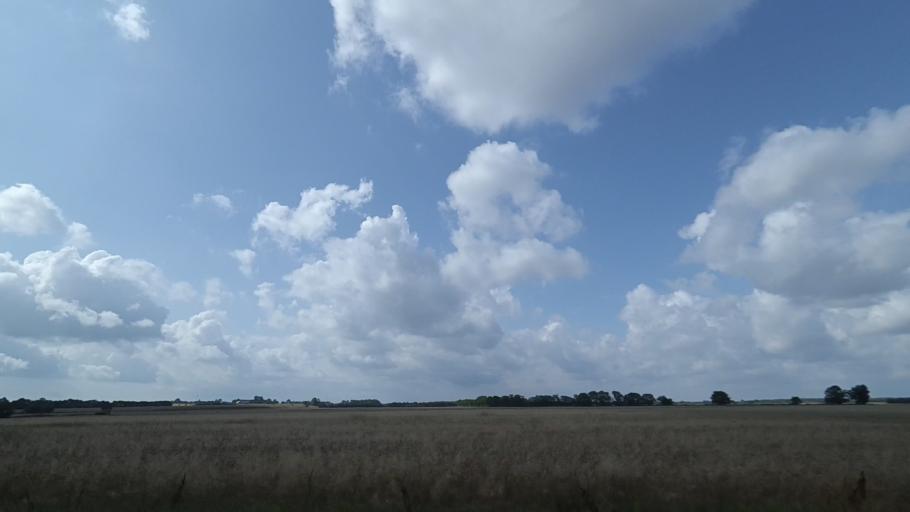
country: DK
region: Central Jutland
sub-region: Norddjurs Kommune
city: Auning
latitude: 56.5025
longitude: 10.4274
